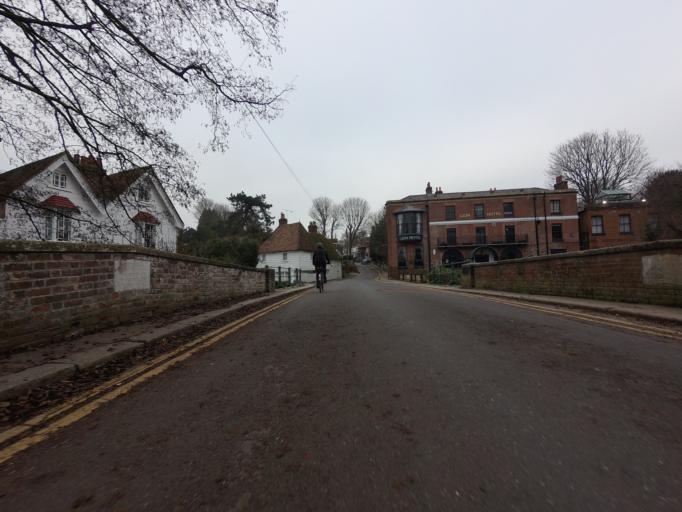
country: GB
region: England
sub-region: Kent
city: Eynsford
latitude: 51.3813
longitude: 0.2204
